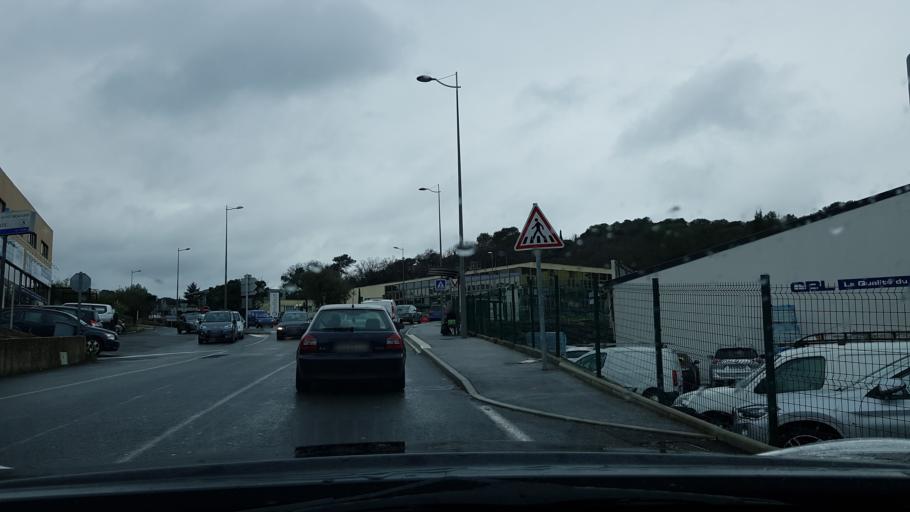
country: FR
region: Provence-Alpes-Cote d'Azur
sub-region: Departement des Alpes-Maritimes
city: Vallauris
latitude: 43.5938
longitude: 7.0571
